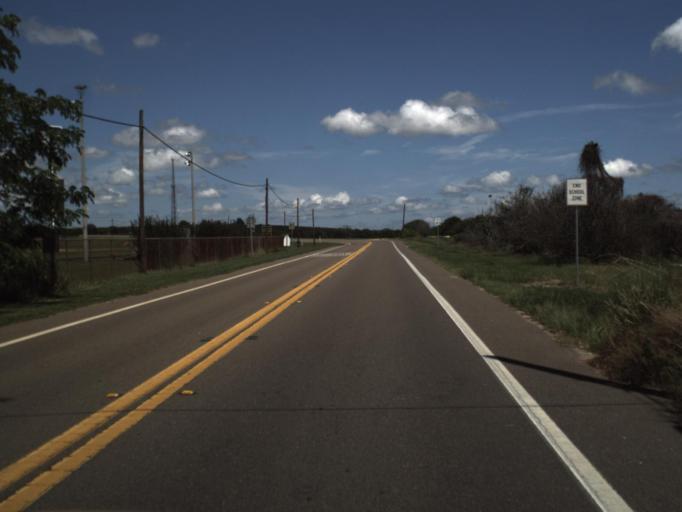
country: US
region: Florida
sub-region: Polk County
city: Frostproof
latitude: 27.7598
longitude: -81.5306
